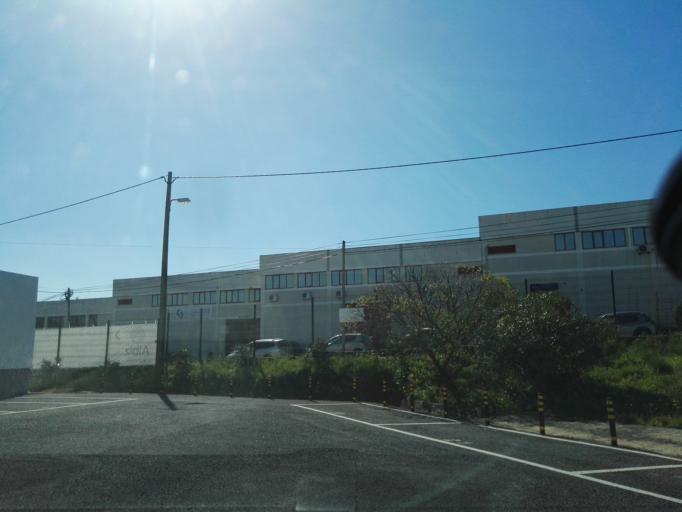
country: PT
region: Lisbon
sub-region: Sintra
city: Rio de Mouro
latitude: 38.7520
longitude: -9.3531
